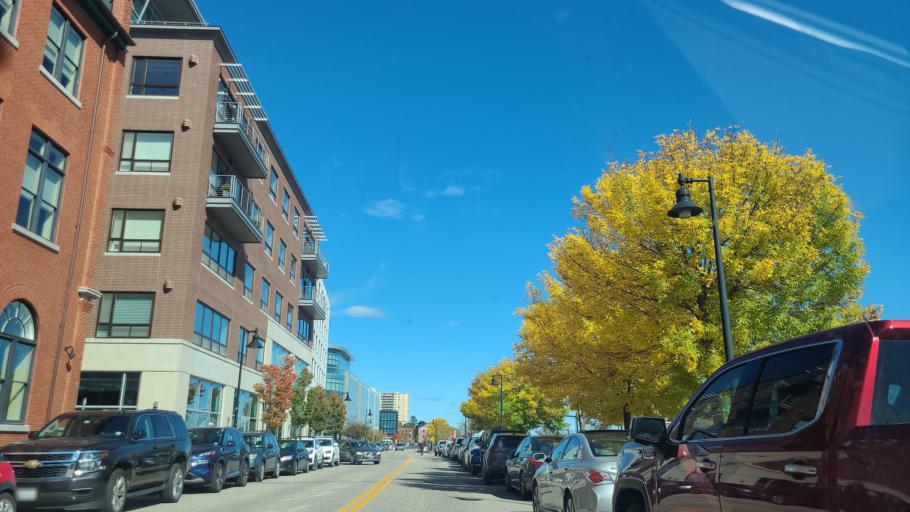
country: US
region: Maine
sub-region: Cumberland County
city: Portland
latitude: 43.6593
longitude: -70.2482
